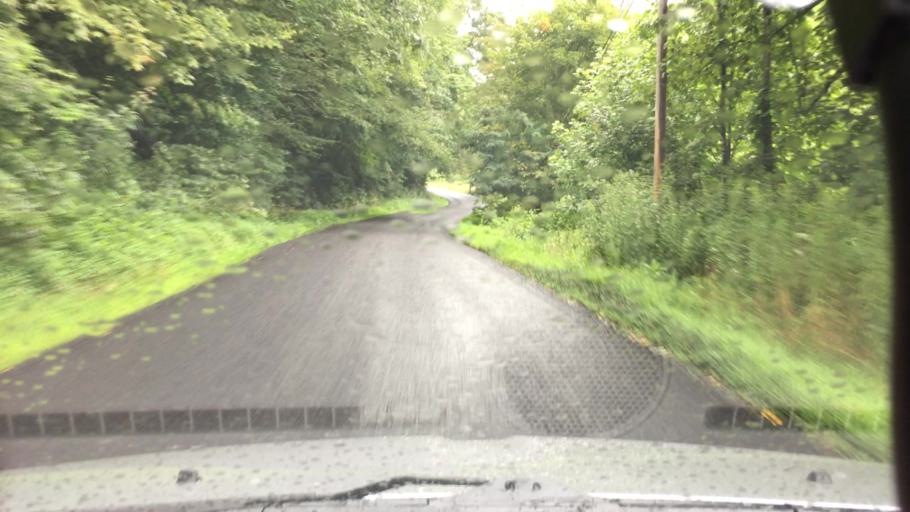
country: US
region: North Carolina
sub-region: Madison County
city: Mars Hill
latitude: 35.9124
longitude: -82.5054
